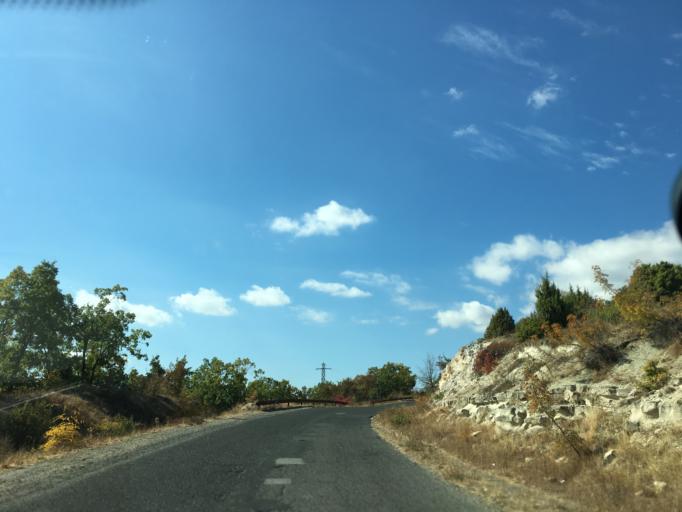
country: BG
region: Kurdzhali
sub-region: Obshtina Krumovgrad
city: Krumovgrad
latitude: 41.5457
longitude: 25.5411
